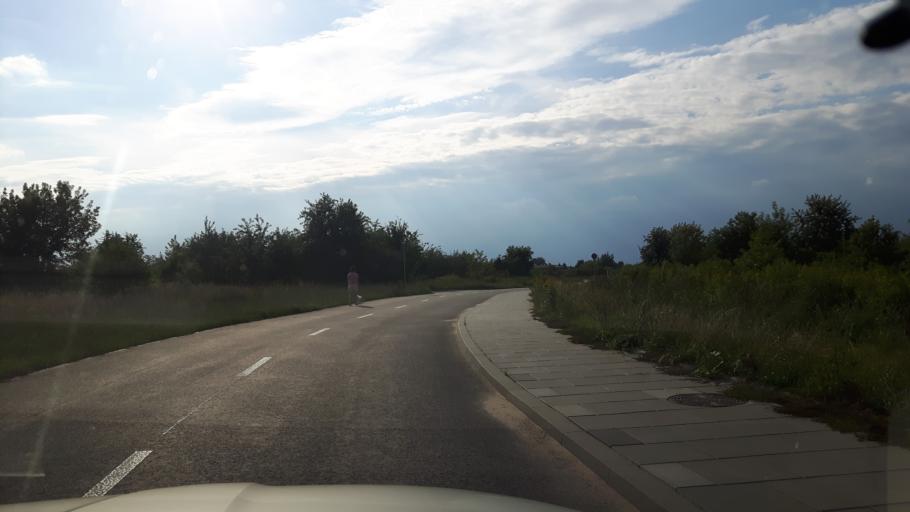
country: PL
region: Masovian Voivodeship
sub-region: Powiat wolominski
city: Marki
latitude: 52.3251
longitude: 21.0862
